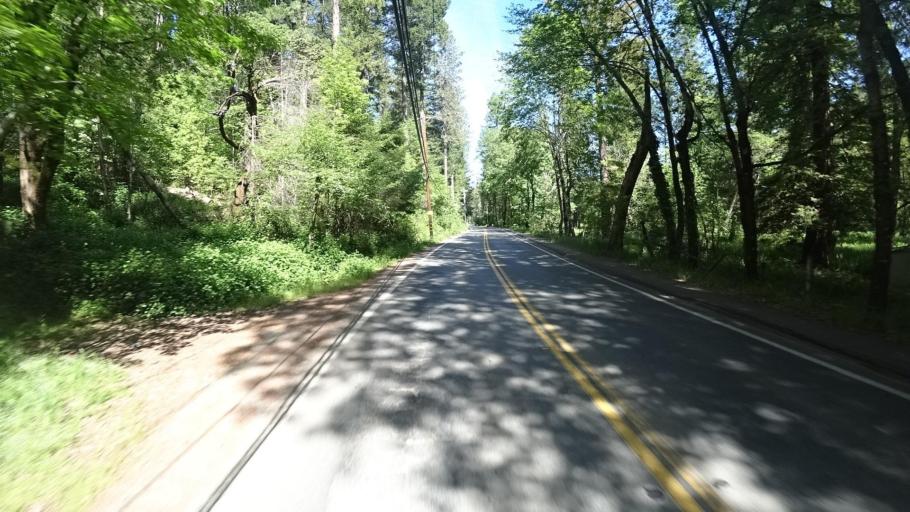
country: US
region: California
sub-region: Lake County
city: Cobb
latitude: 38.8245
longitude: -122.7239
